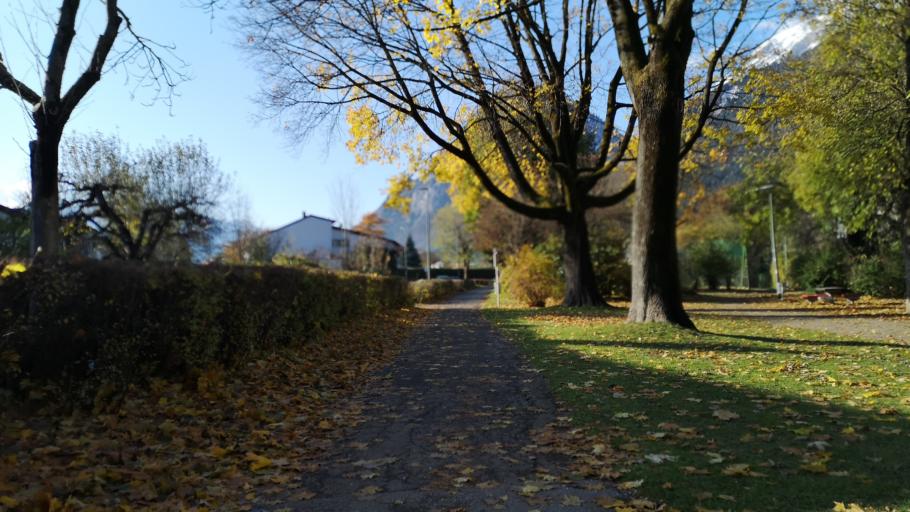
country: AT
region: Tyrol
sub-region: Innsbruck Stadt
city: Innsbruck
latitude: 47.2631
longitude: 11.3665
